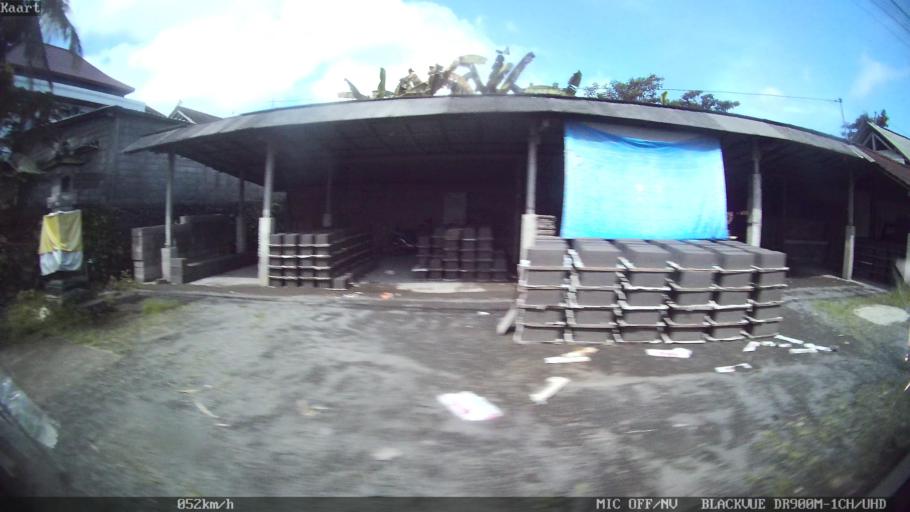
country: ID
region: Bali
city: Banjar Kelodan
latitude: -8.5222
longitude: 115.3298
